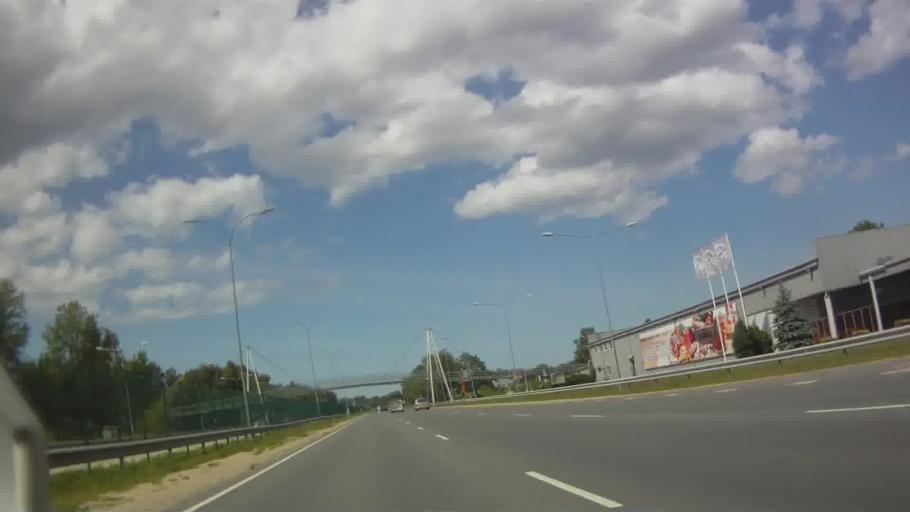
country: LV
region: Marupe
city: Marupe
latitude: 56.9393
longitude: 24.0005
